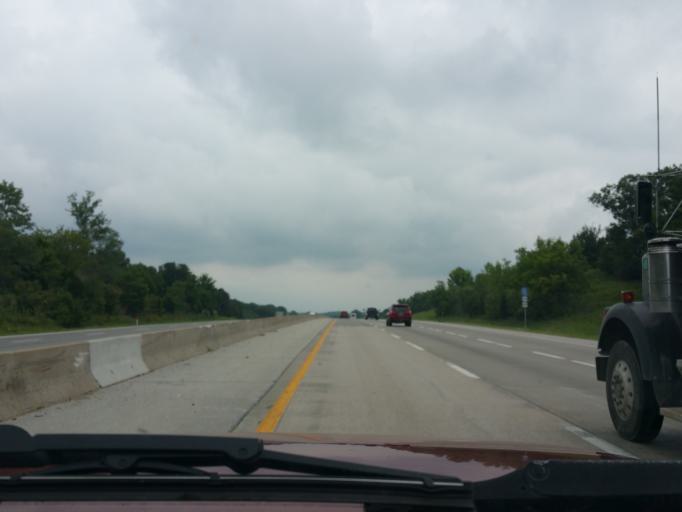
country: US
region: Kansas
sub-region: Wyandotte County
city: Edwardsville
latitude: 39.1054
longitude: -94.7945
